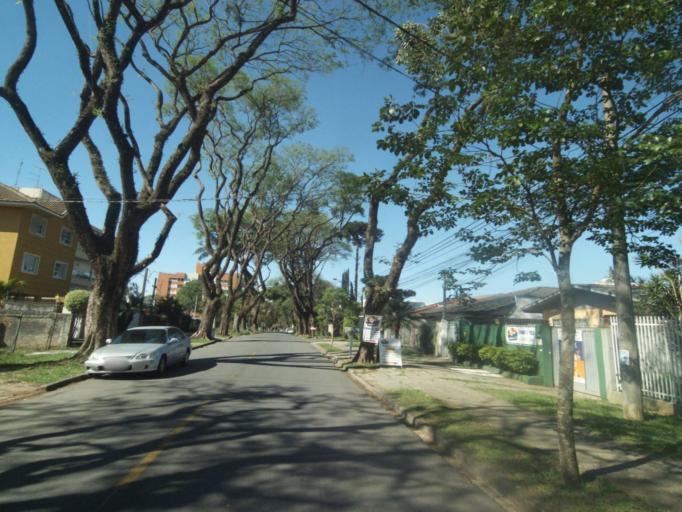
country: BR
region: Parana
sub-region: Curitiba
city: Curitiba
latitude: -25.3921
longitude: -49.2363
